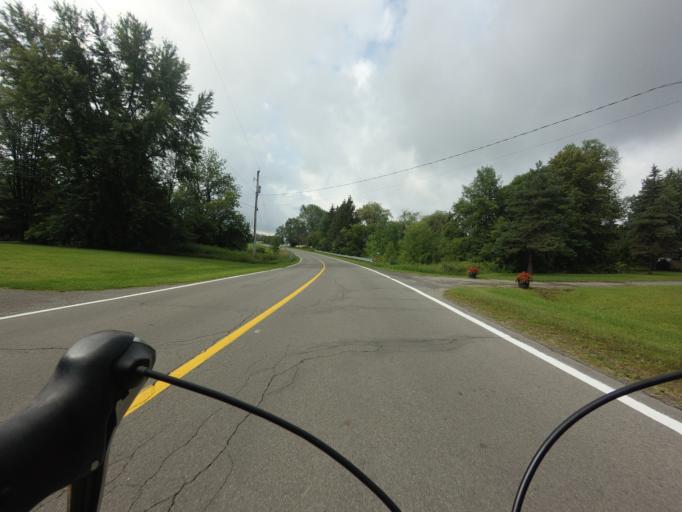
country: CA
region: Ontario
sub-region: Lanark County
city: Smiths Falls
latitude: 44.9723
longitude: -75.8082
